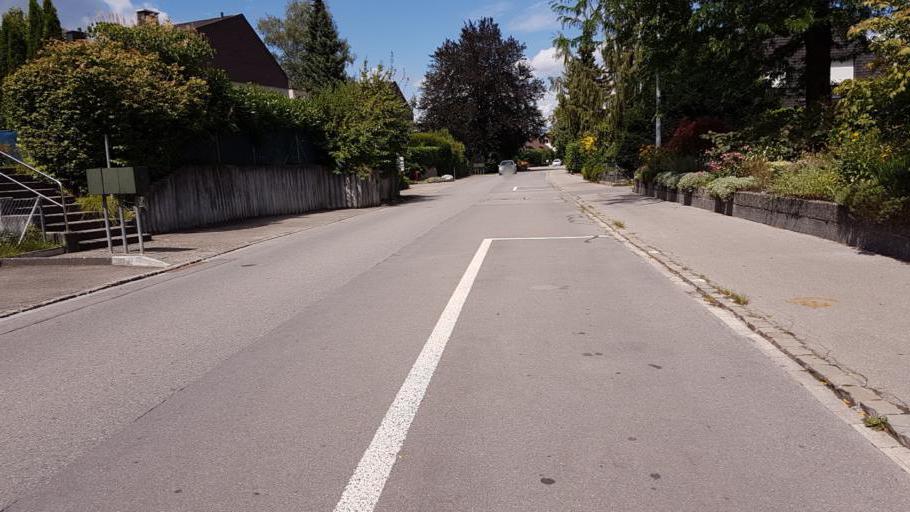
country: CH
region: Bern
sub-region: Bern-Mittelland District
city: Munsingen
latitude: 46.8704
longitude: 7.5501
